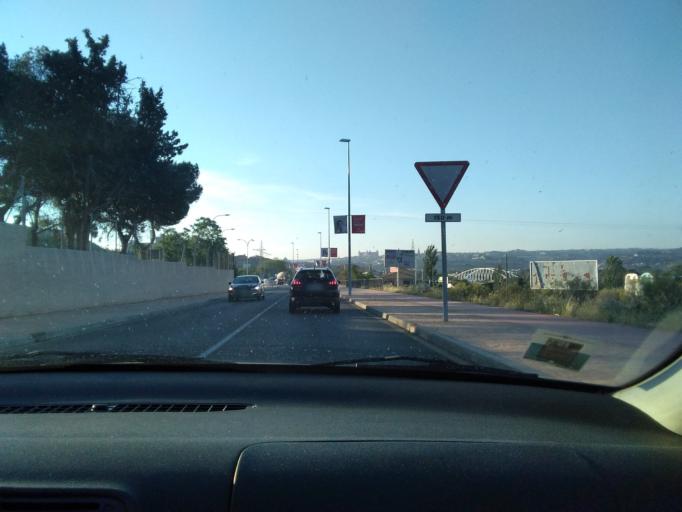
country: ES
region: Castille-La Mancha
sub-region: Province of Toledo
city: Toledo
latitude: 39.8801
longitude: -4.0494
